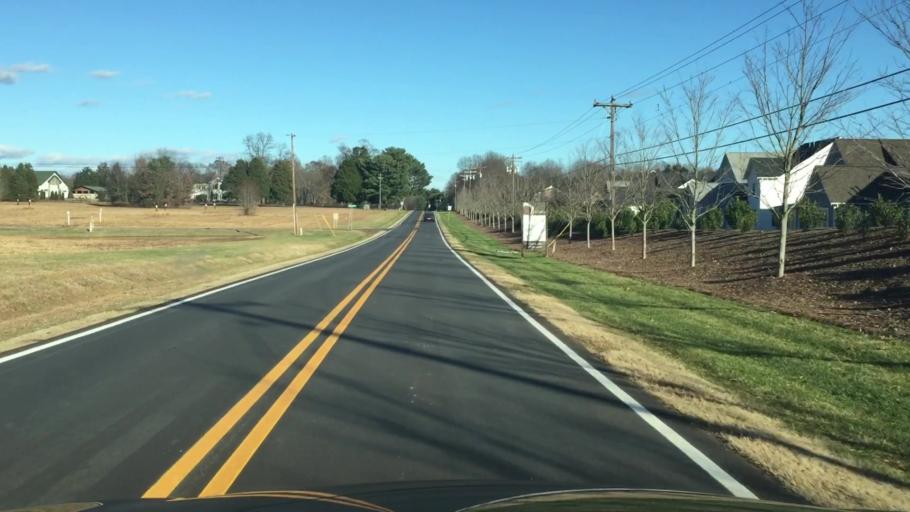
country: US
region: North Carolina
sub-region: Mecklenburg County
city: Cornelius
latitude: 35.5251
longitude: -80.8789
